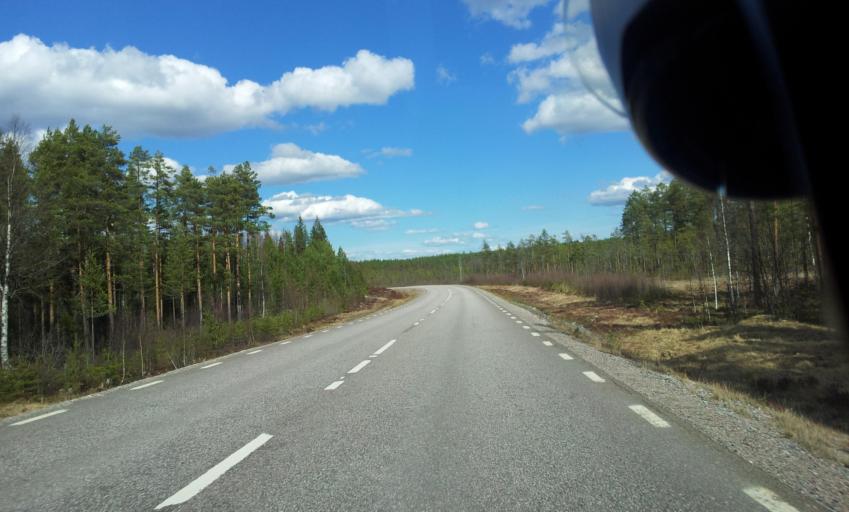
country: SE
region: Gaevleborg
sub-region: Ovanakers Kommun
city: Edsbyn
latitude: 61.2795
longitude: 15.8988
